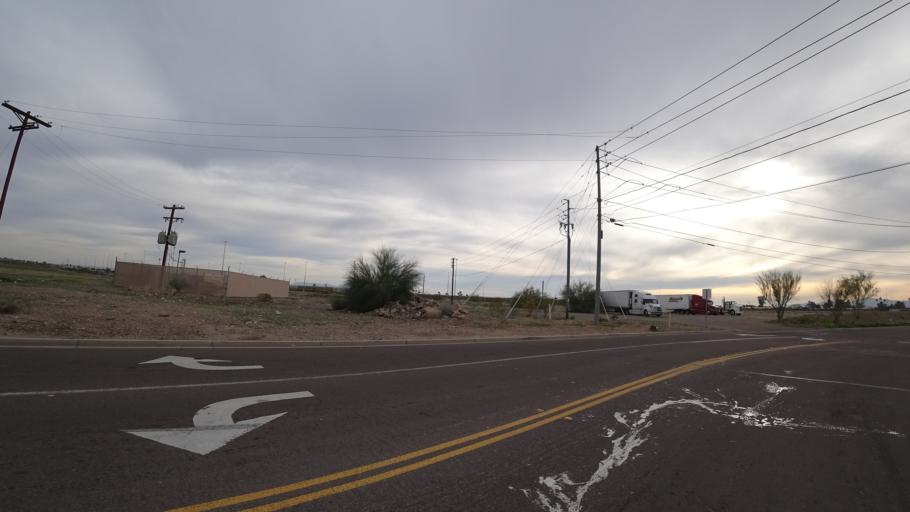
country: US
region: Arizona
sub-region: Maricopa County
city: El Mirage
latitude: 33.6235
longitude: -112.3244
